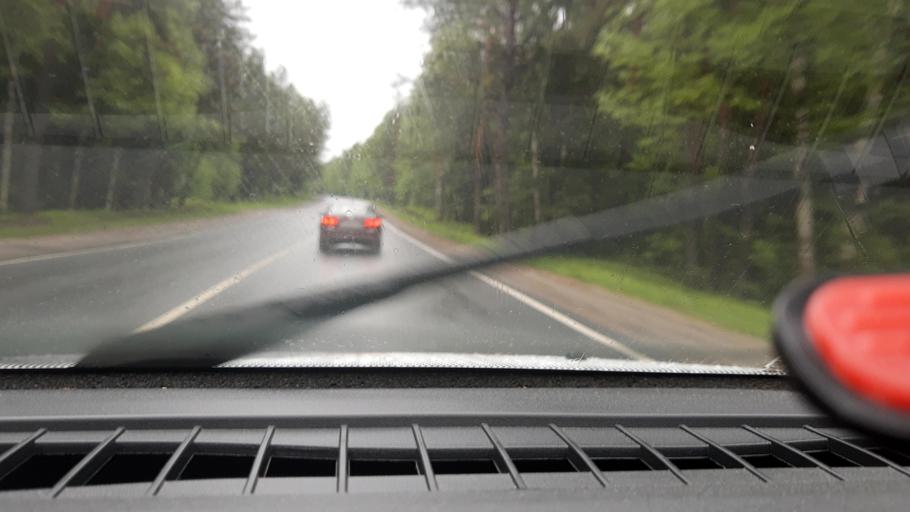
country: RU
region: Nizjnij Novgorod
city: Semenov
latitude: 56.7424
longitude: 44.3484
